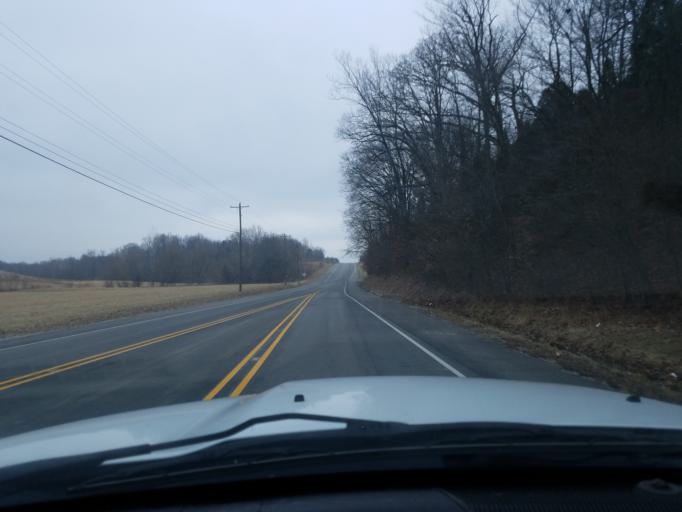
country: US
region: Indiana
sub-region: Perry County
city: Tell City
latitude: 37.9658
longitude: -86.7445
